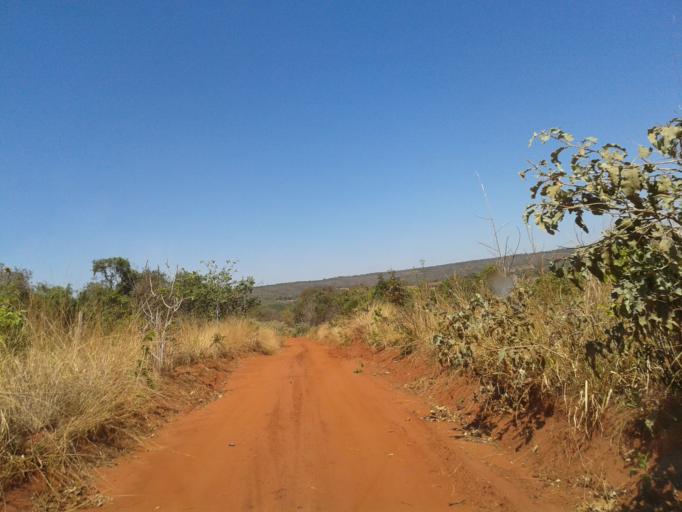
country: BR
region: Minas Gerais
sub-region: Ituiutaba
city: Ituiutaba
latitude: -19.1062
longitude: -49.2712
